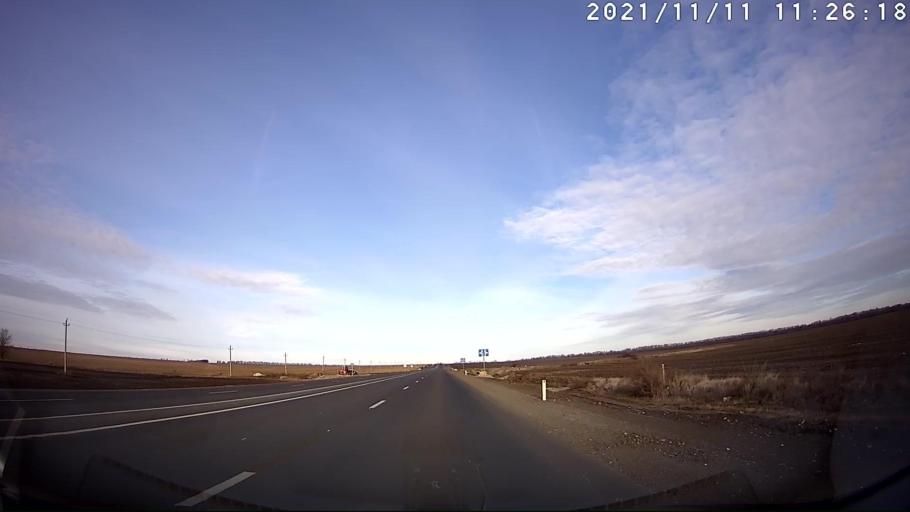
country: RU
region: Samara
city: Syzran'
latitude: 53.2328
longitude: 48.4935
